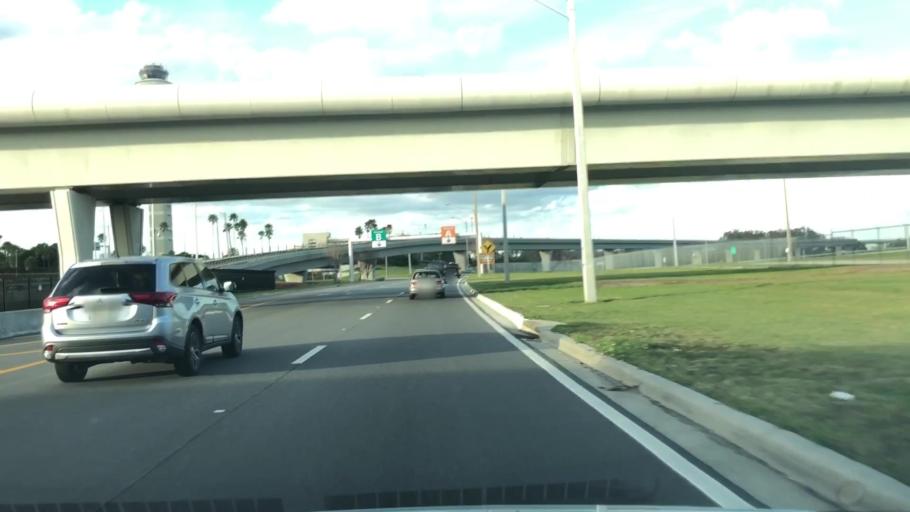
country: US
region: Florida
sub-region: Orange County
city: Taft
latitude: 28.4238
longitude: -81.3064
